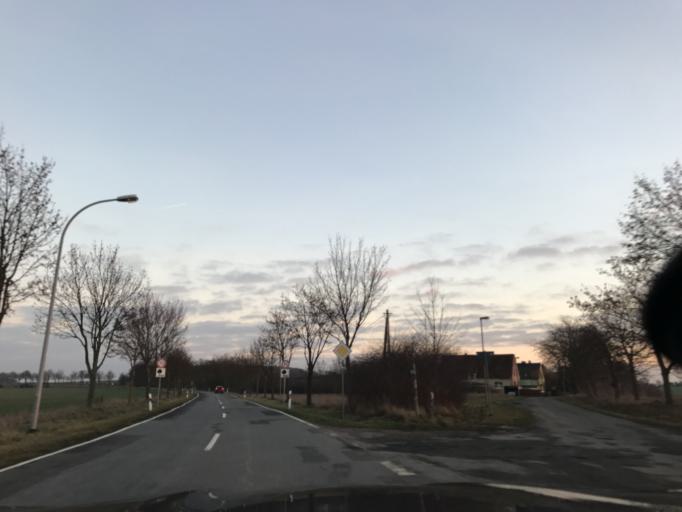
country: DE
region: Brandenburg
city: Pawesin
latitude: 52.5103
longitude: 12.6483
